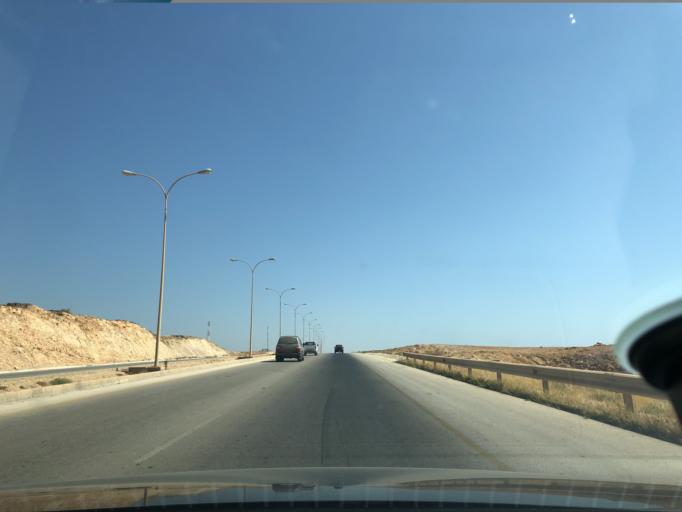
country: OM
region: Zufar
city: Salalah
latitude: 17.0512
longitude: 54.3132
